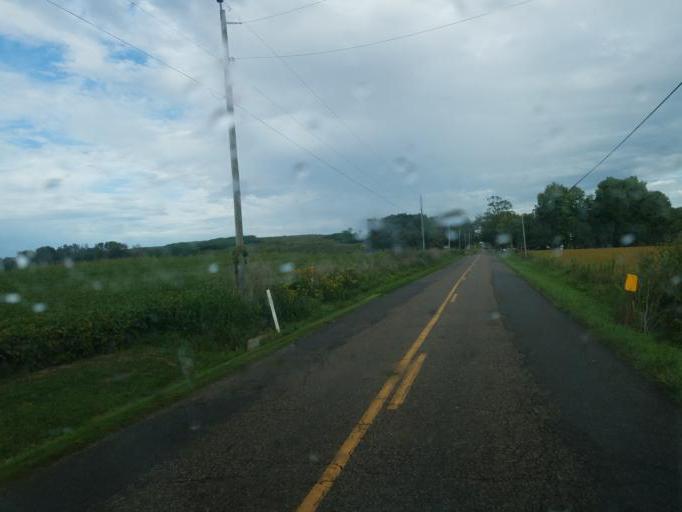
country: US
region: Ohio
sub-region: Knox County
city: Centerburg
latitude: 40.3219
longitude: -82.7323
